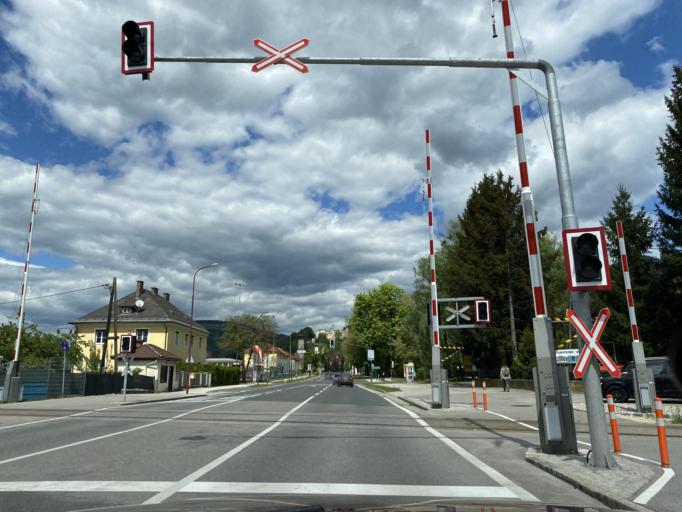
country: AT
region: Carinthia
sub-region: Politischer Bezirk Wolfsberg
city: Wolfsberg
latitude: 46.8314
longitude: 14.8416
